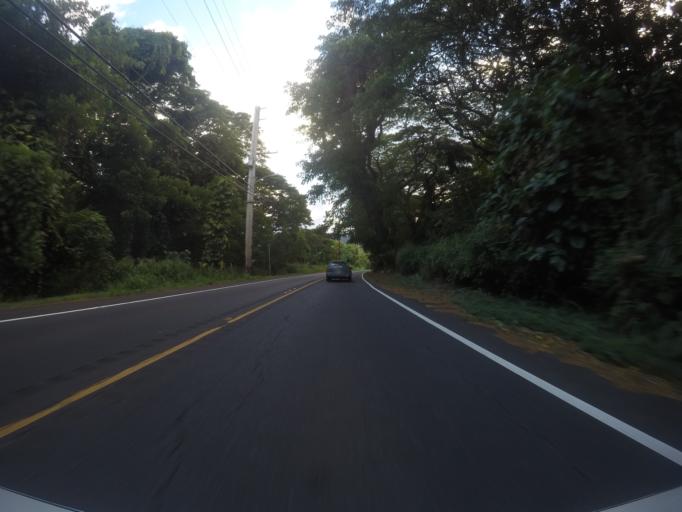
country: US
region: Hawaii
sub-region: Honolulu County
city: Ka'a'awa
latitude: 21.5158
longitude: -157.8412
